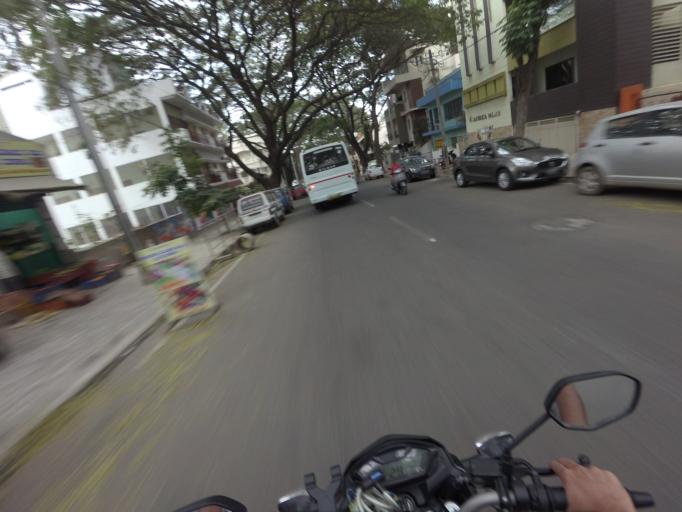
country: IN
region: Karnataka
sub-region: Bangalore Urban
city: Bangalore
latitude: 12.9639
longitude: 77.5410
